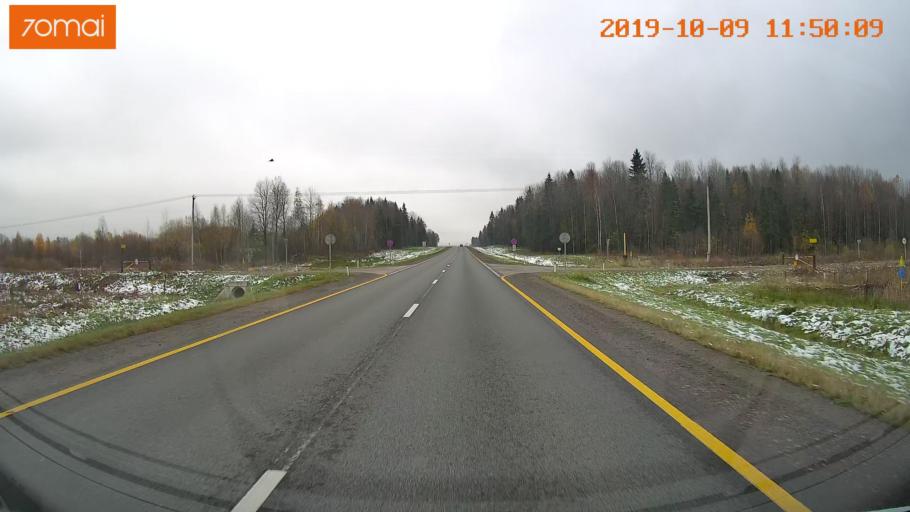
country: RU
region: Vologda
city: Gryazovets
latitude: 58.8093
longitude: 40.2416
